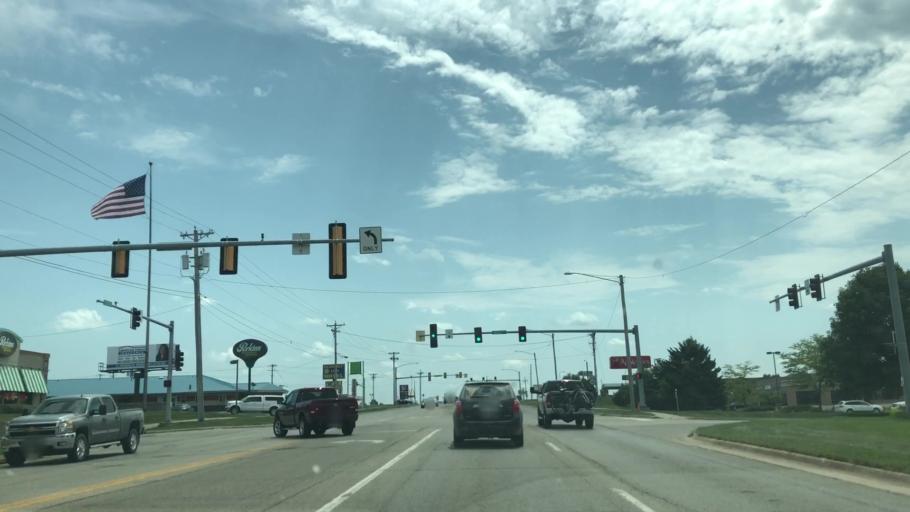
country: US
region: Iowa
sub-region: Marshall County
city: Marshalltown
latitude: 42.0090
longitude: -92.9124
